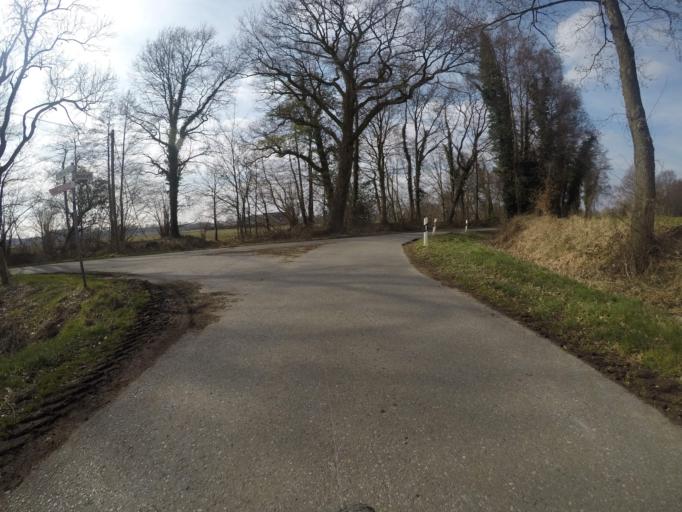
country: DE
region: North Rhine-Westphalia
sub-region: Regierungsbezirk Munster
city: Rhede
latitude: 51.8116
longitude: 6.7002
